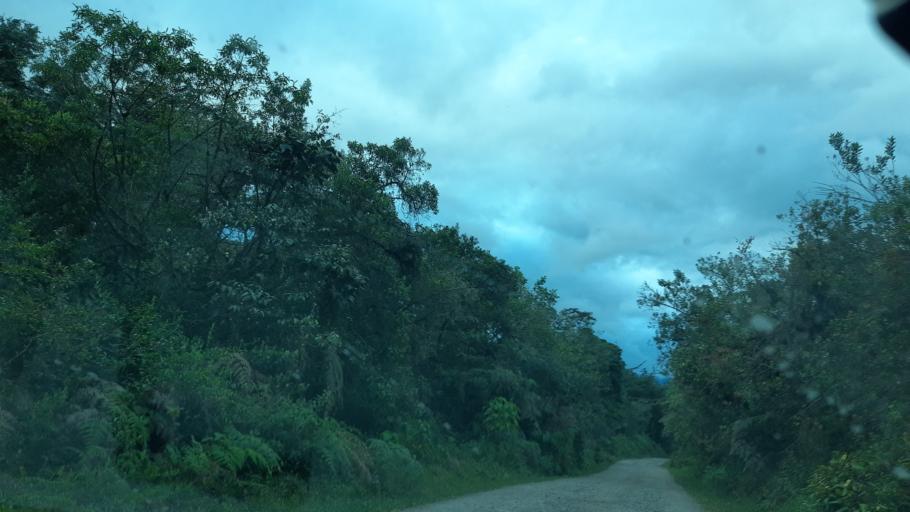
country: CO
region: Boyaca
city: Garagoa
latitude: 5.0895
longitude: -73.3298
